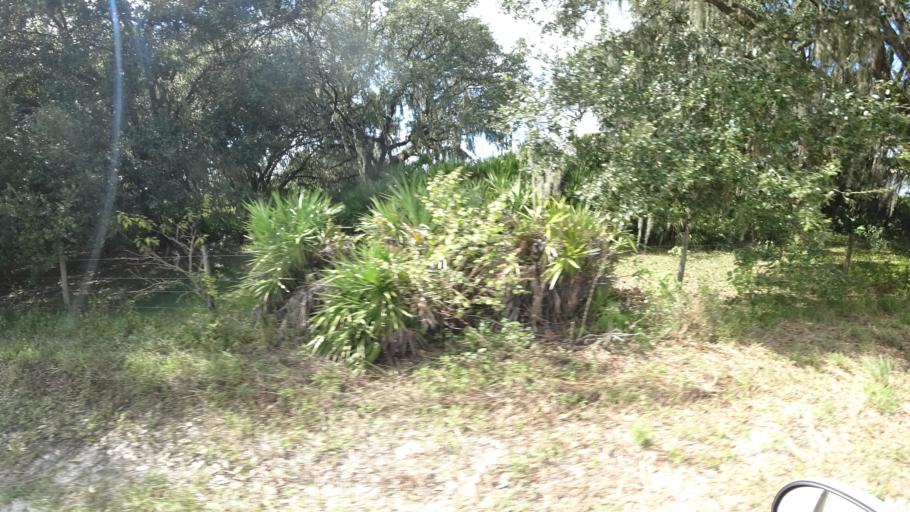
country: US
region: Florida
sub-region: DeSoto County
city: Arcadia
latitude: 27.3356
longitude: -82.1050
